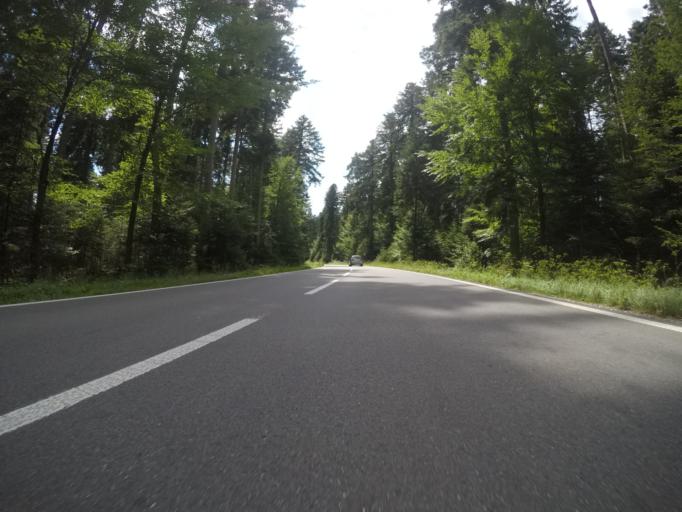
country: DE
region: Baden-Wuerttemberg
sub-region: Karlsruhe Region
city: Neubulach
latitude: 48.6415
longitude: 8.6668
